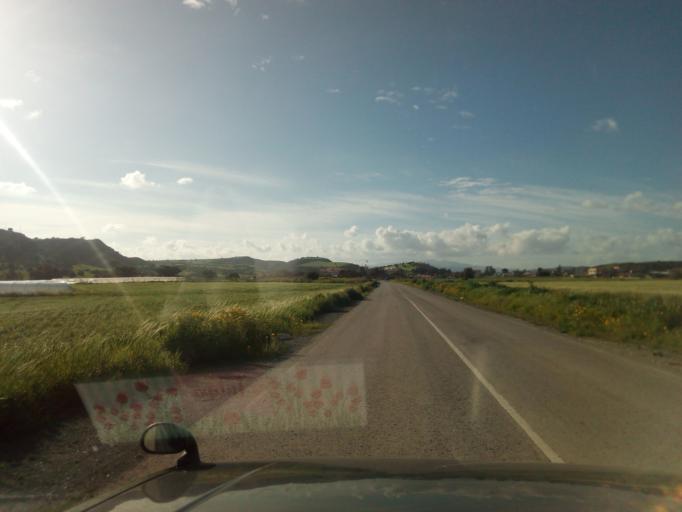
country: CY
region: Larnaka
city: Kofinou
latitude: 34.8037
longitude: 33.4428
